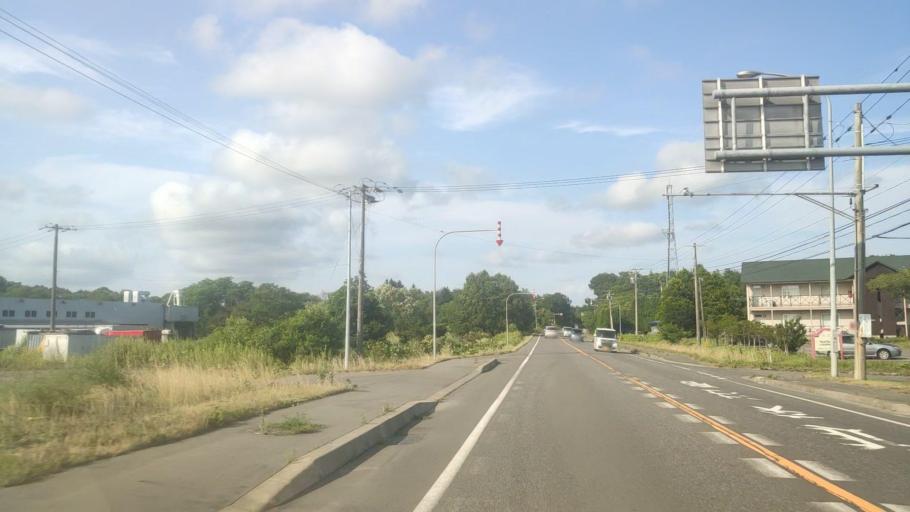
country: JP
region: Hokkaido
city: Chitose
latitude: 42.7328
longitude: 141.7755
